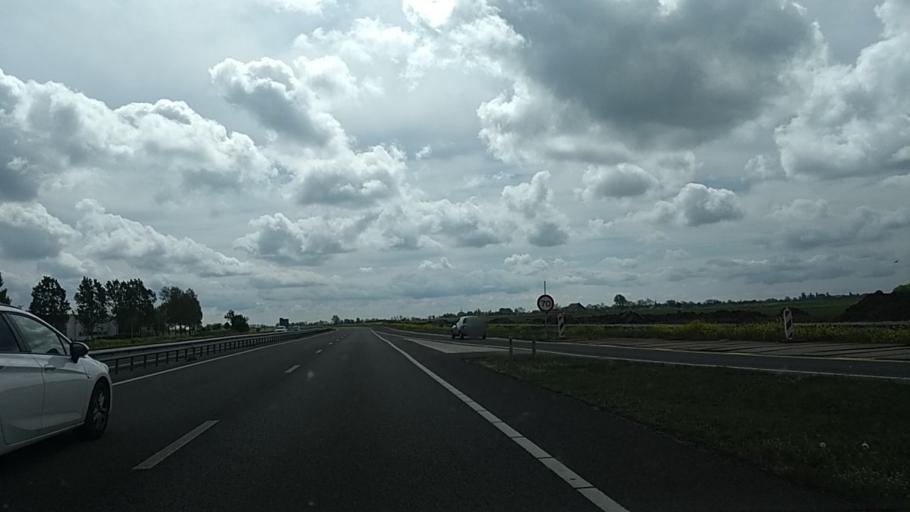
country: NL
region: Friesland
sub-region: Sudwest Fryslan
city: IJlst
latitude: 53.0321
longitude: 5.6230
